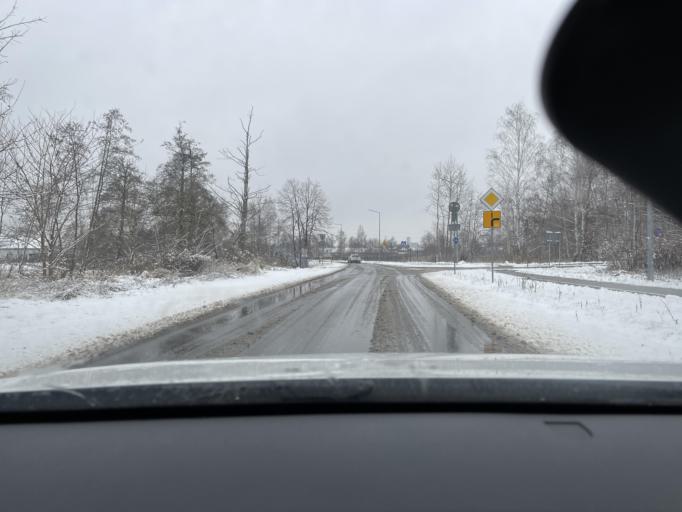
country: PL
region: Masovian Voivodeship
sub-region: Powiat zyrardowski
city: Zyrardow
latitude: 52.0388
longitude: 20.4483
